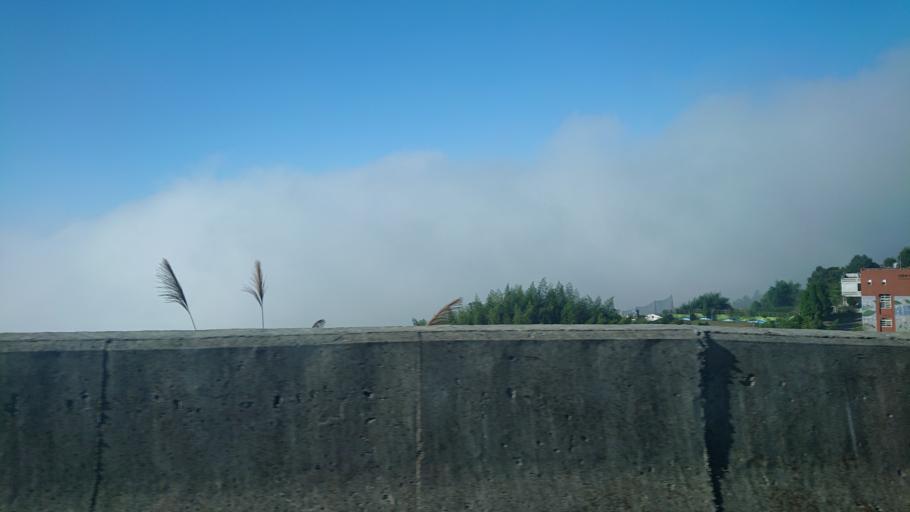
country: TW
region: Taiwan
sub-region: Chiayi
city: Jiayi Shi
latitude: 23.4775
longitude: 120.6989
